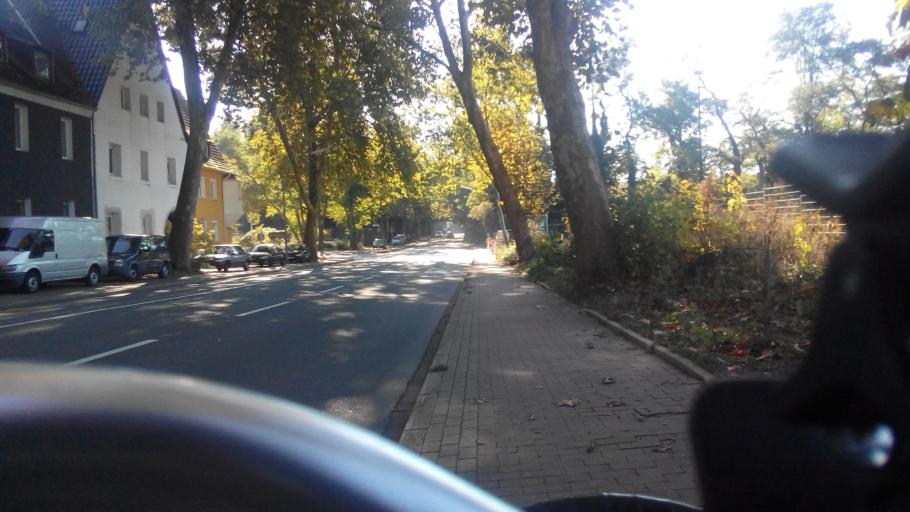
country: DE
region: North Rhine-Westphalia
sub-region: Regierungsbezirk Munster
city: Gelsenkirchen
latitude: 51.5169
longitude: 7.1345
